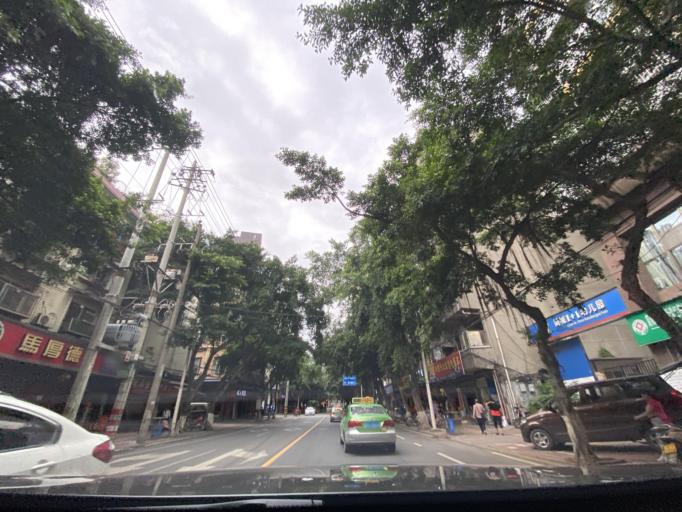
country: CN
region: Sichuan
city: Jiancheng
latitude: 30.3847
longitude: 104.5526
